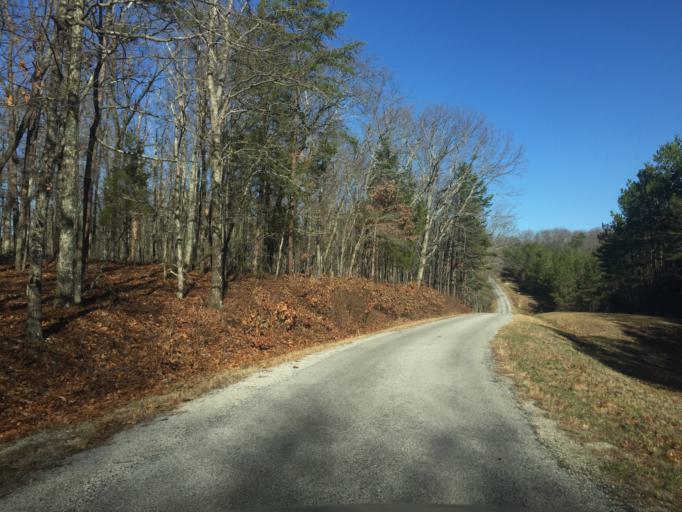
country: US
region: Tennessee
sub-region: Hamilton County
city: Harrison
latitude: 35.0951
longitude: -85.1008
